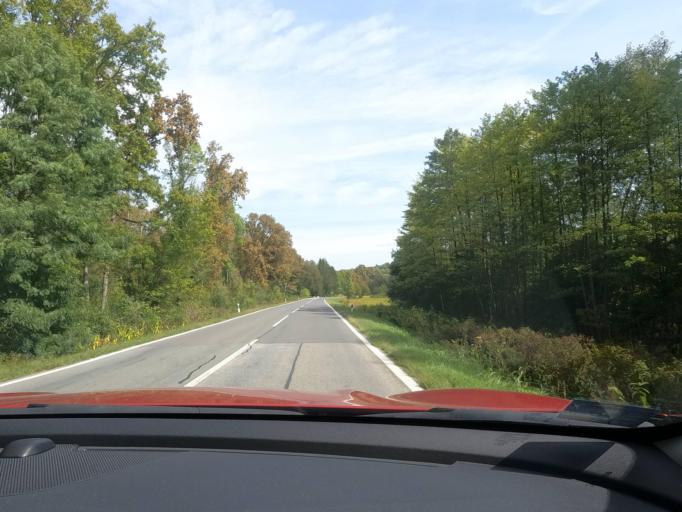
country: HR
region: Sisacko-Moslavacka
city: Budasevo
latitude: 45.4896
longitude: 16.4862
